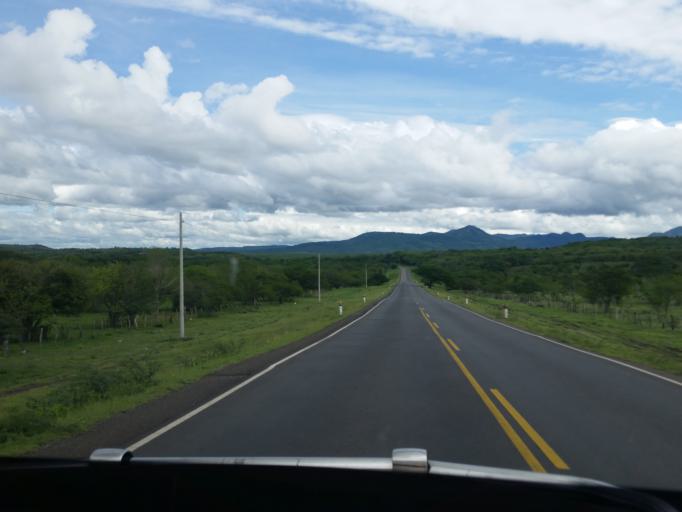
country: NI
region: Matagalpa
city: Ciudad Dario
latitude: 12.6830
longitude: -86.0865
